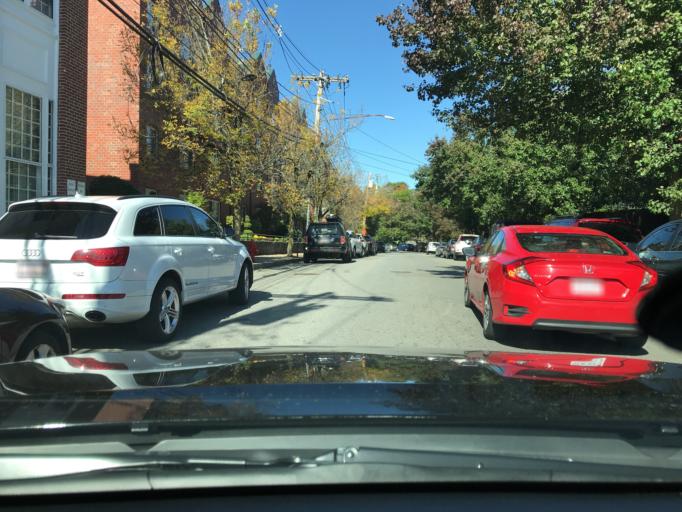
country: US
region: Massachusetts
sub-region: Middlesex County
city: Newton
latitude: 42.3309
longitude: -71.1922
